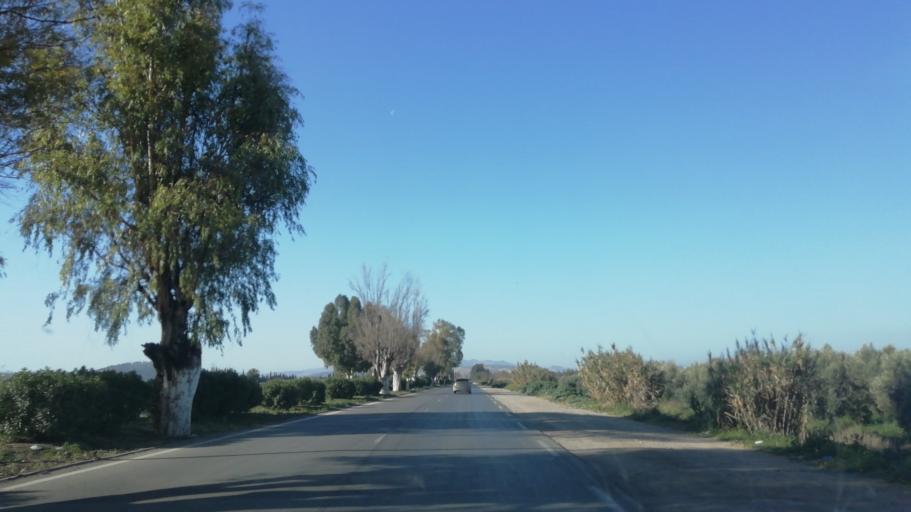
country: DZ
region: Mascara
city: Mascara
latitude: 35.6075
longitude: 0.0936
